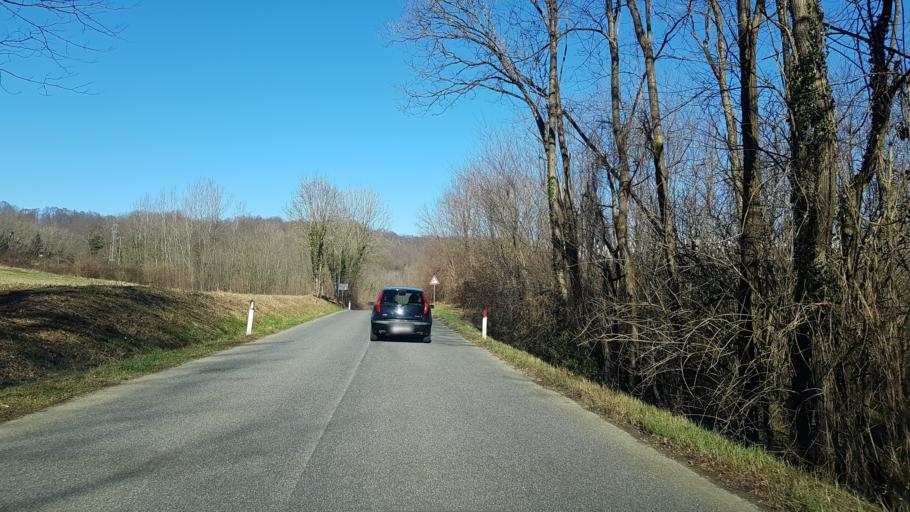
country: IT
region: Friuli Venezia Giulia
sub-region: Provincia di Udine
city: Attimis
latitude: 46.1712
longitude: 13.2938
